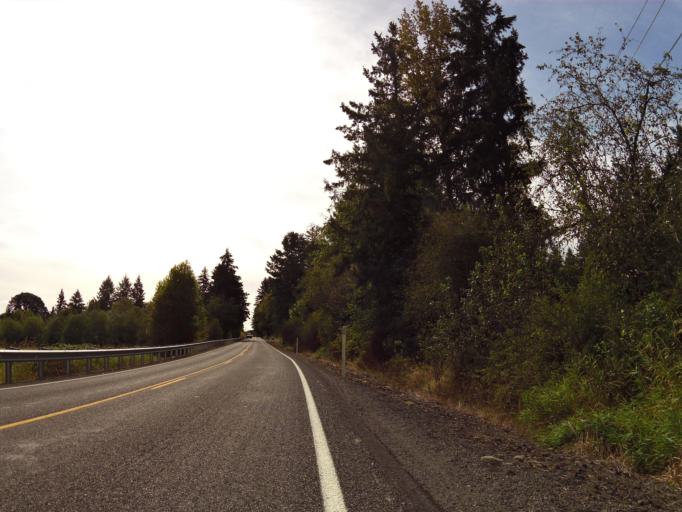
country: US
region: Washington
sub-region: Lewis County
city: Chehalis
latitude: 46.6358
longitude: -122.9713
